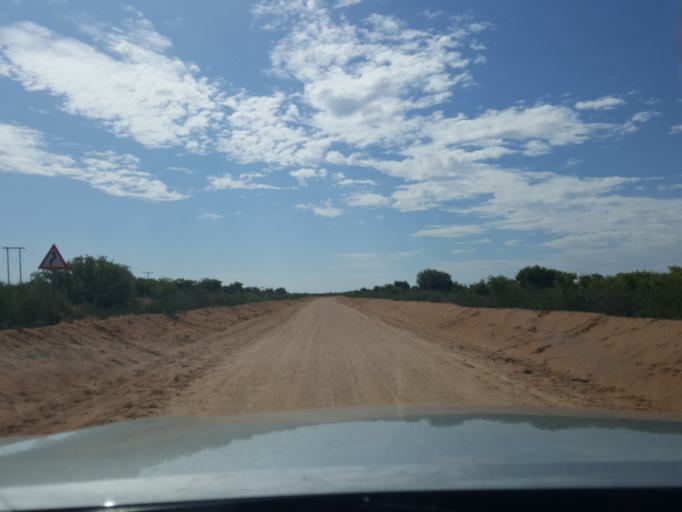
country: BW
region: Kweneng
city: Khudumelapye
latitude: -23.8544
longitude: 24.8762
